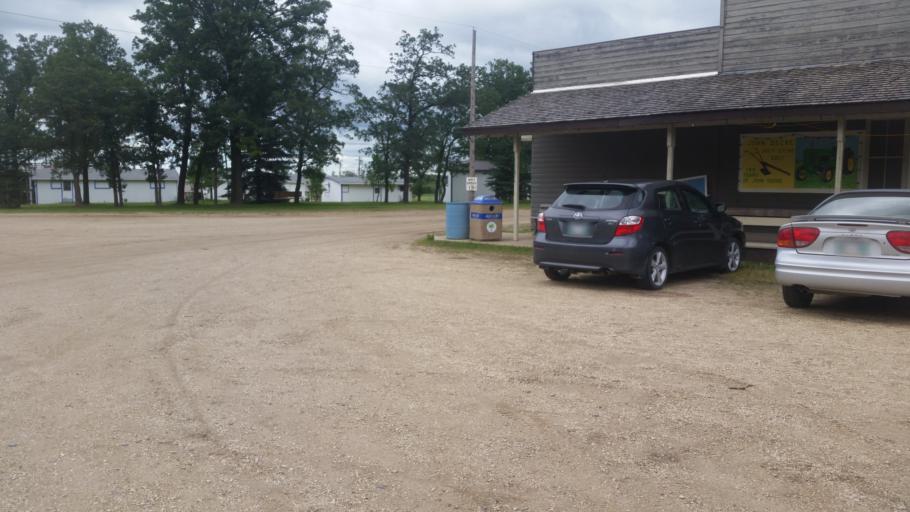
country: CA
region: Manitoba
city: Carberry
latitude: 49.9254
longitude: -98.9476
